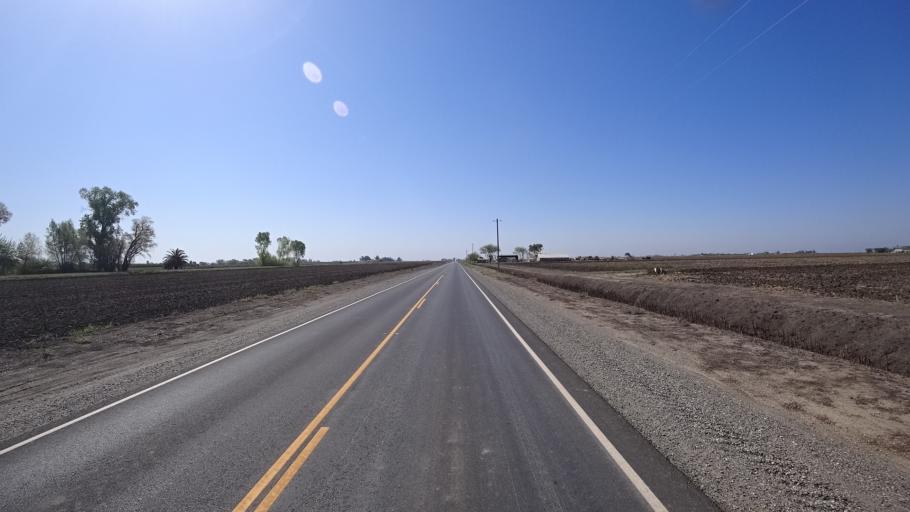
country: US
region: California
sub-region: Glenn County
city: Hamilton City
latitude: 39.6149
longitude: -122.0650
